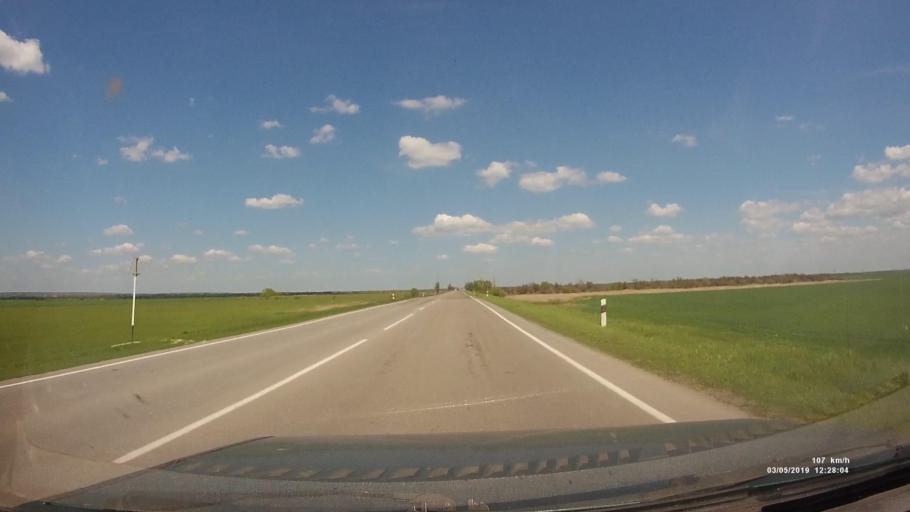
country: RU
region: Rostov
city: Semikarakorsk
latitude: 47.4678
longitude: 40.7254
